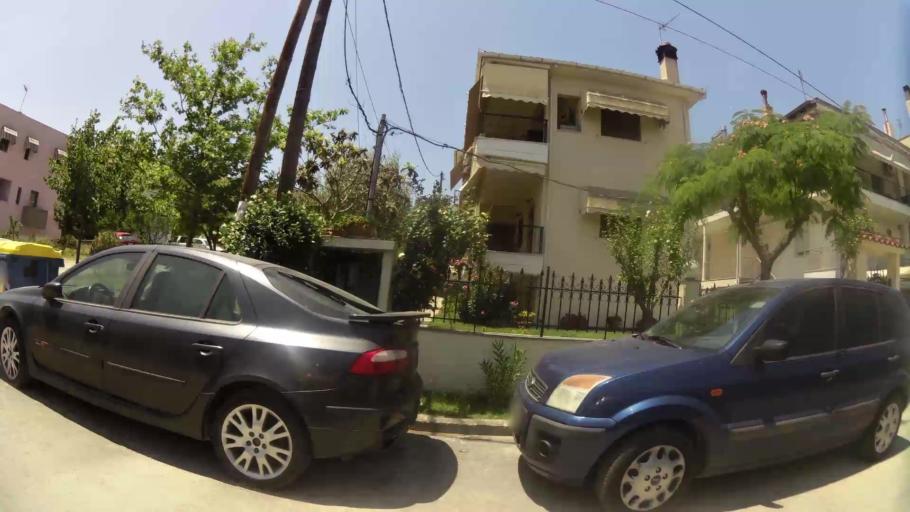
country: GR
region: Central Macedonia
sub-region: Nomos Thessalonikis
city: Plagiari
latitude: 40.4697
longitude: 22.9574
